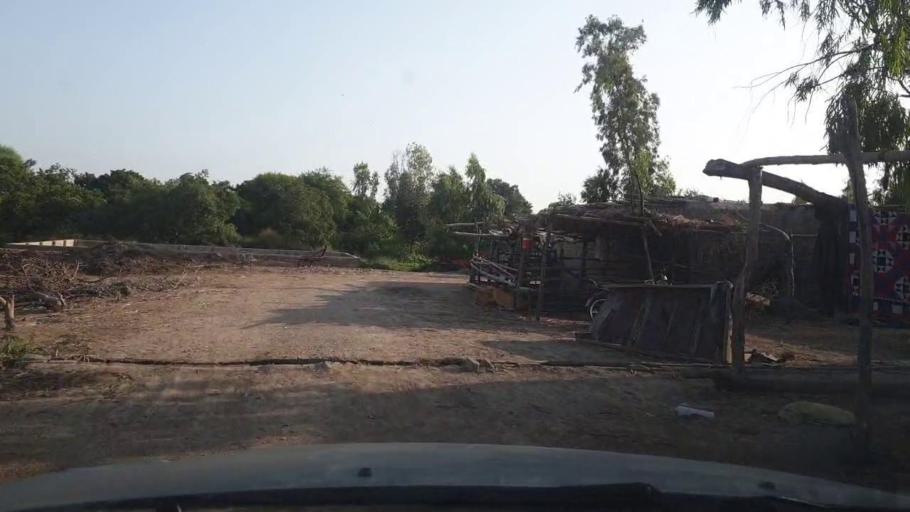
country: PK
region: Sindh
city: Tando Ghulam Ali
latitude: 25.1641
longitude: 68.9574
